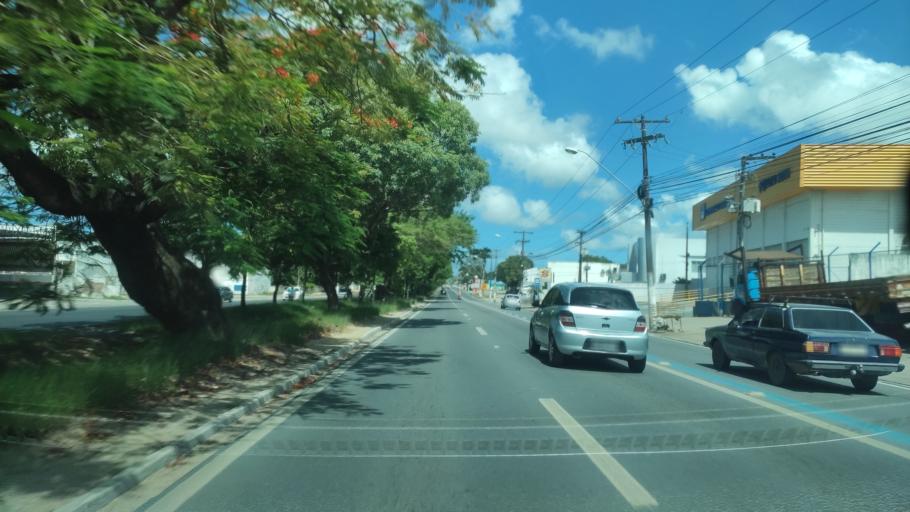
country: BR
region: Alagoas
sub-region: Satuba
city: Satuba
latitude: -9.5798
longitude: -35.7681
